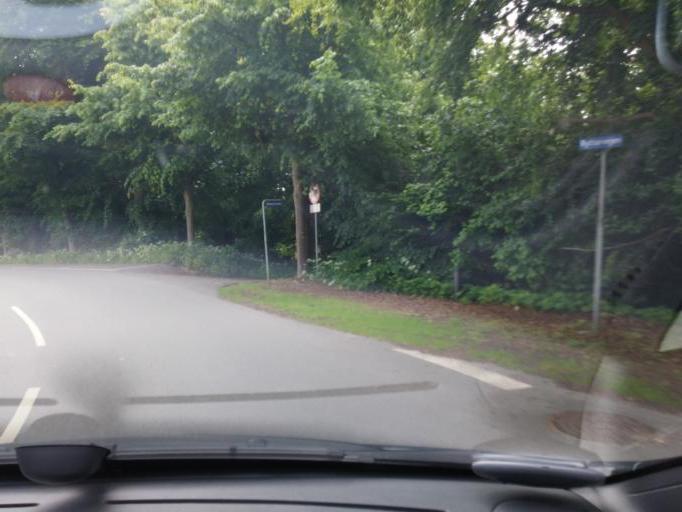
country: DK
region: South Denmark
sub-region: Odense Kommune
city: Bullerup
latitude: 55.3994
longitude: 10.4636
